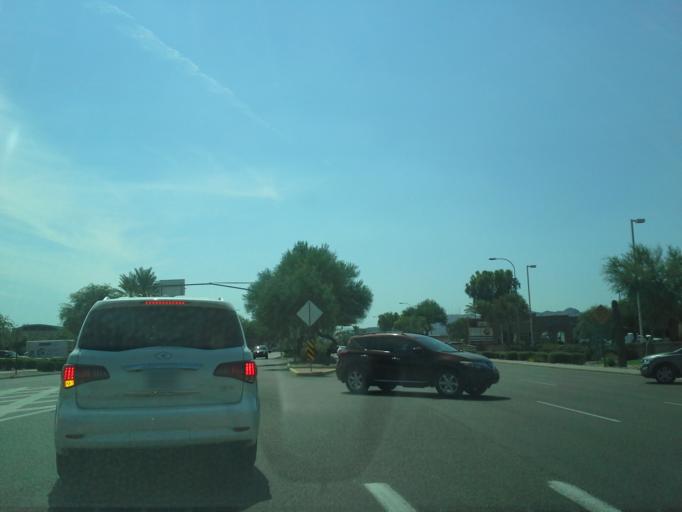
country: US
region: Arizona
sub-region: Maricopa County
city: Guadalupe
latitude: 33.3199
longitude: -111.9779
